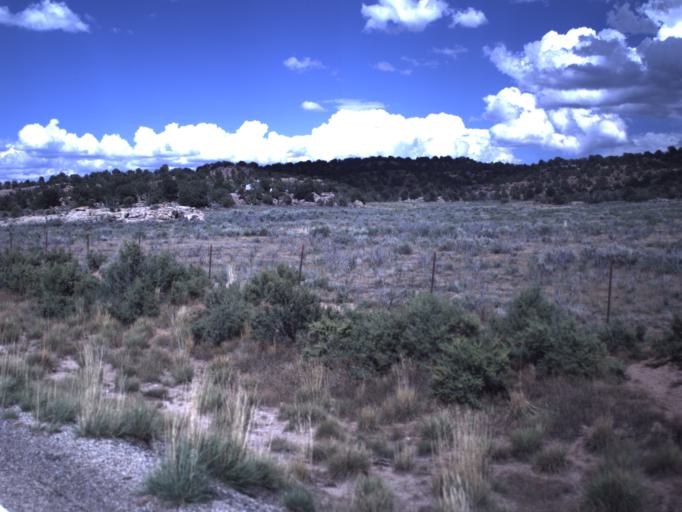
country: US
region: Utah
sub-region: Duchesne County
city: Duchesne
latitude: 40.2287
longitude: -110.7206
